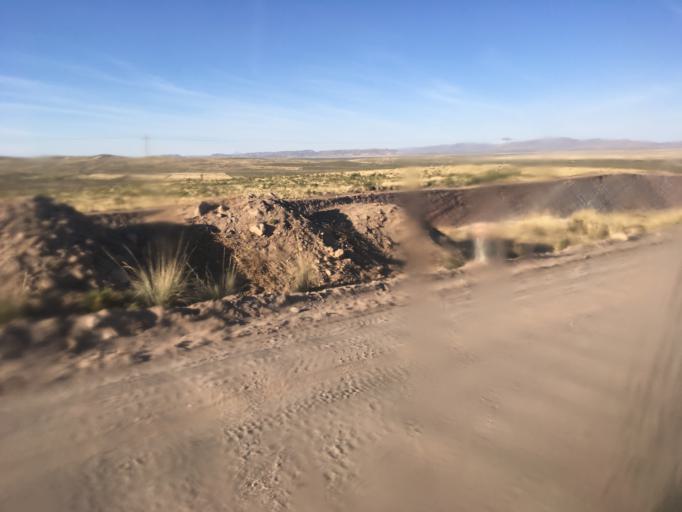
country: PE
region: Puno
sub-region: Provincia de Chucuito
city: Kelluyo
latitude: -16.9833
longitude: -69.0307
